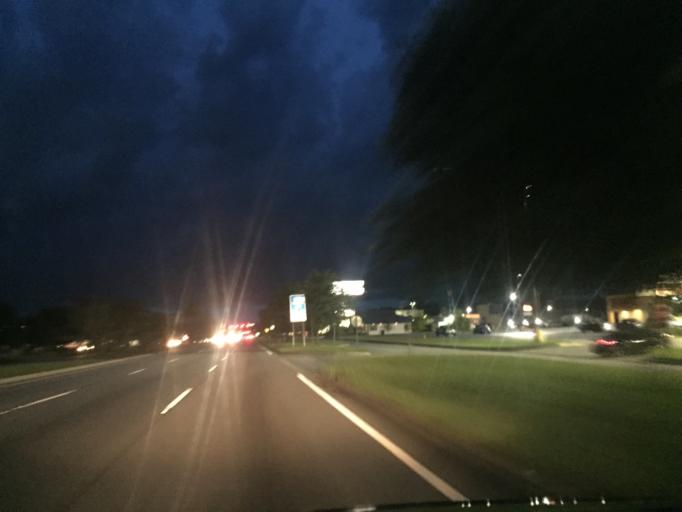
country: US
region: Georgia
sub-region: Chatham County
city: Montgomery
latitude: 31.9823
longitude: -81.1517
